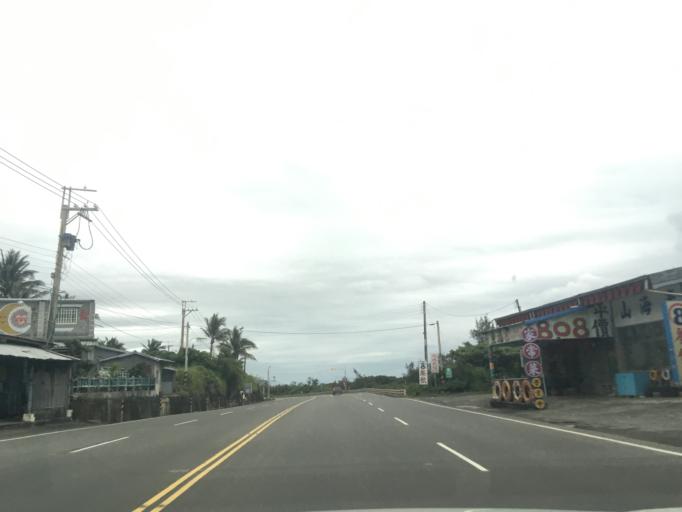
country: TW
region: Taiwan
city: Hengchun
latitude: 22.3036
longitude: 120.8891
